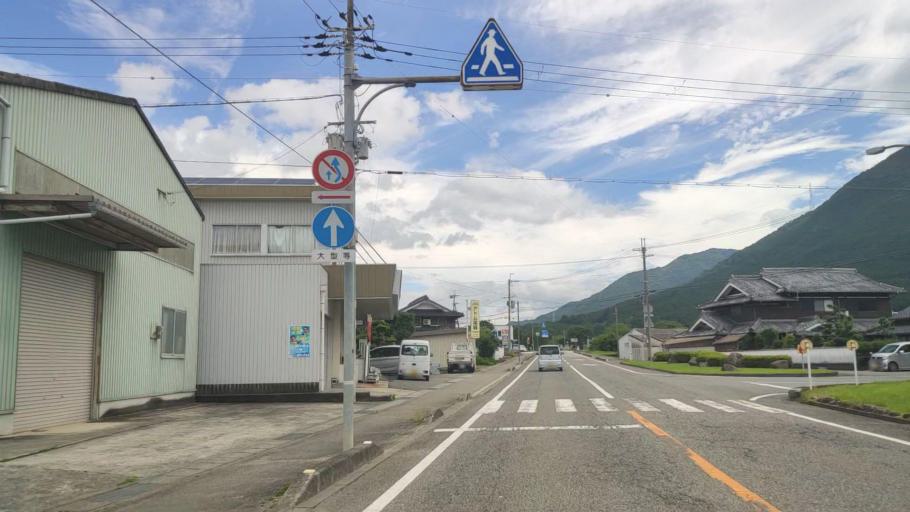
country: JP
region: Hyogo
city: Nishiwaki
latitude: 35.1377
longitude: 134.9252
